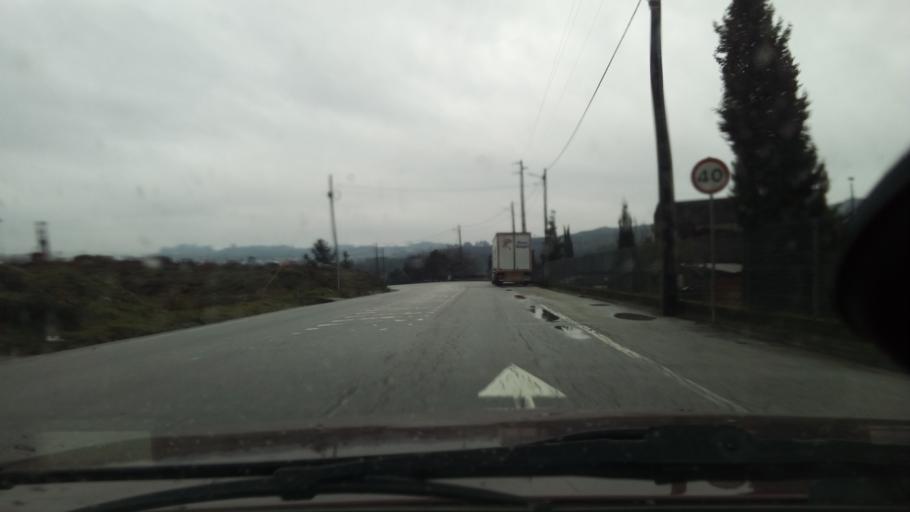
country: PT
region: Viseu
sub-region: Mangualde
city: Mangualde
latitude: 40.6211
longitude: -7.8013
